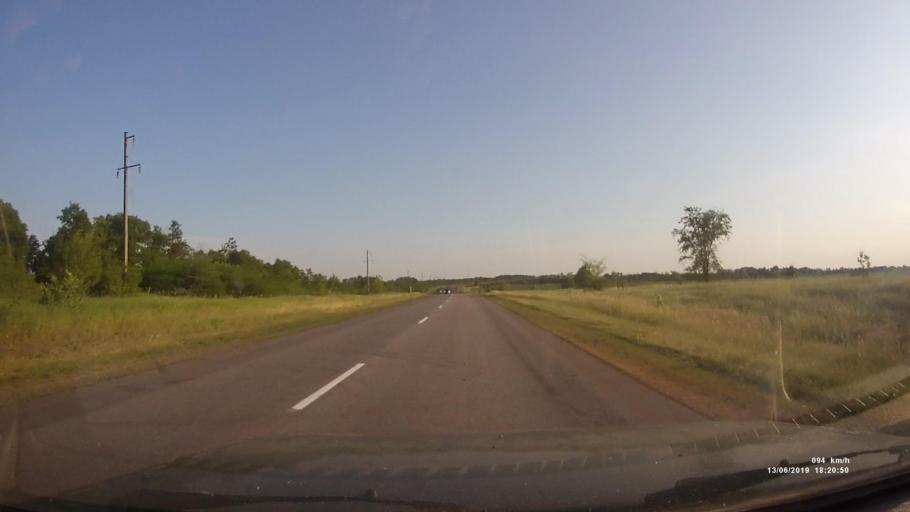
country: RU
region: Rostov
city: Kazanskaya
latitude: 49.8784
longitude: 41.2960
